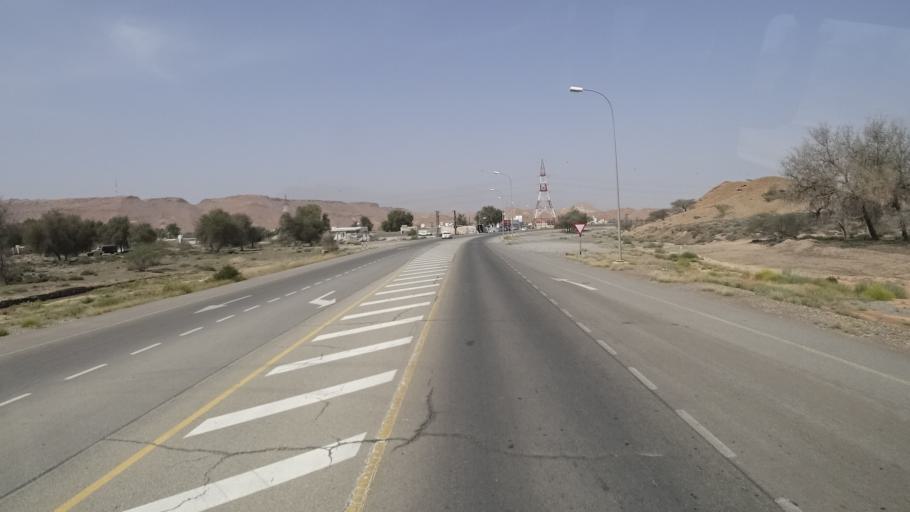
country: OM
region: Muhafazat Masqat
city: Muscat
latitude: 23.2048
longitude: 58.9549
